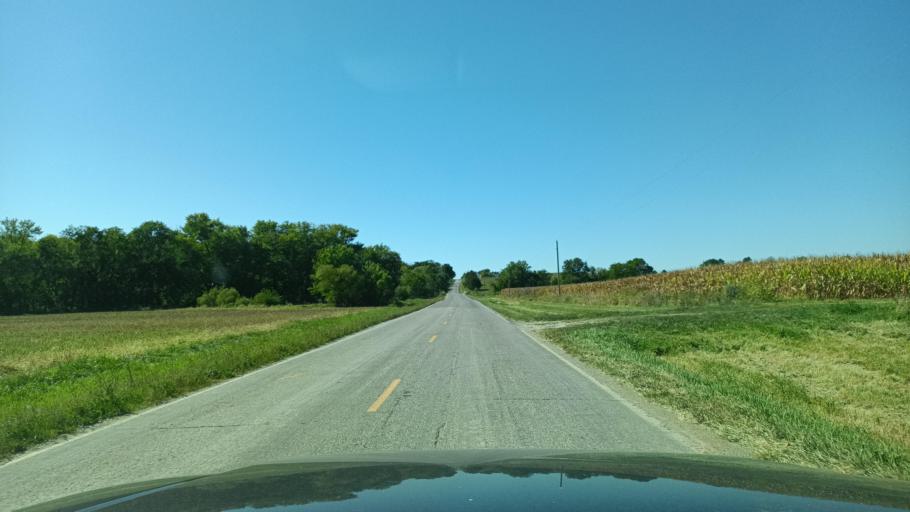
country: US
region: Missouri
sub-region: Macon County
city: La Plata
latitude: 40.0219
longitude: -92.5385
